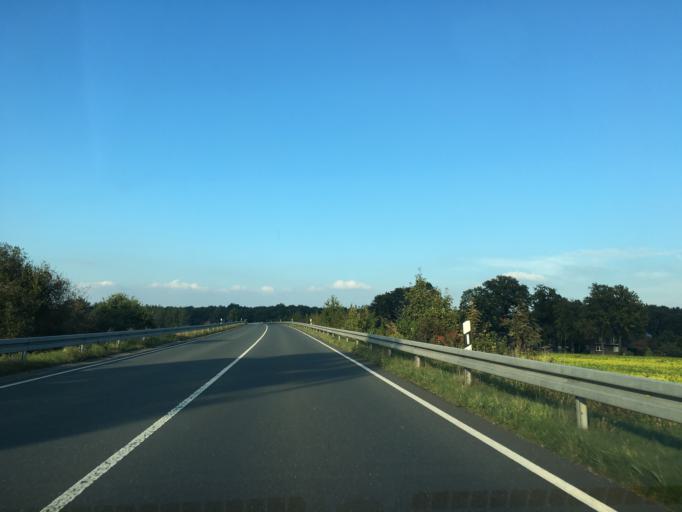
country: DE
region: North Rhine-Westphalia
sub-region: Regierungsbezirk Munster
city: Dulmen
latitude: 51.8047
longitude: 7.3405
